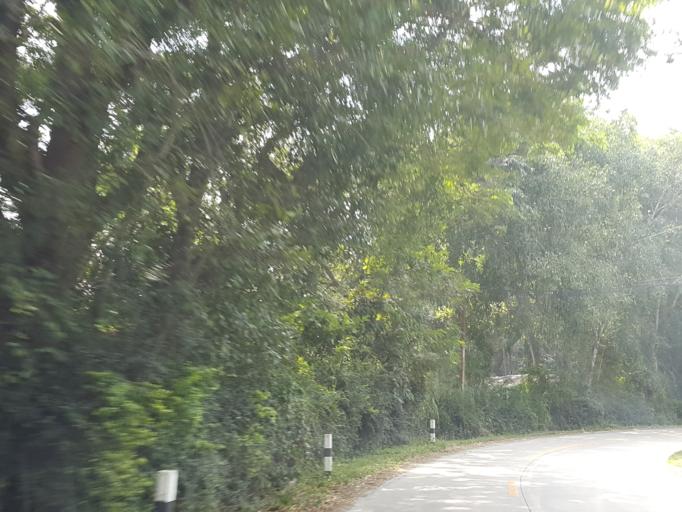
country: TH
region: Chiang Mai
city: Mae On
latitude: 18.8160
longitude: 99.2252
